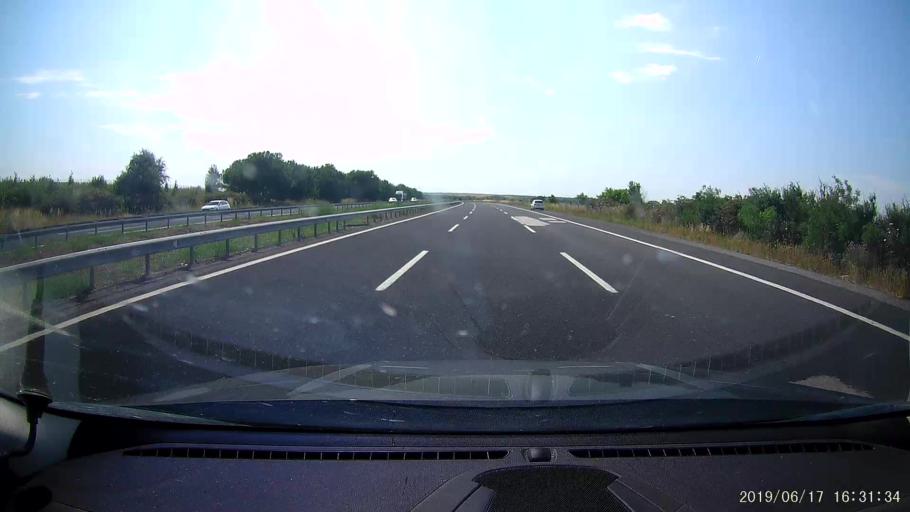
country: TR
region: Tekirdag
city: Beyazkoy
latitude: 41.3629
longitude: 27.6241
